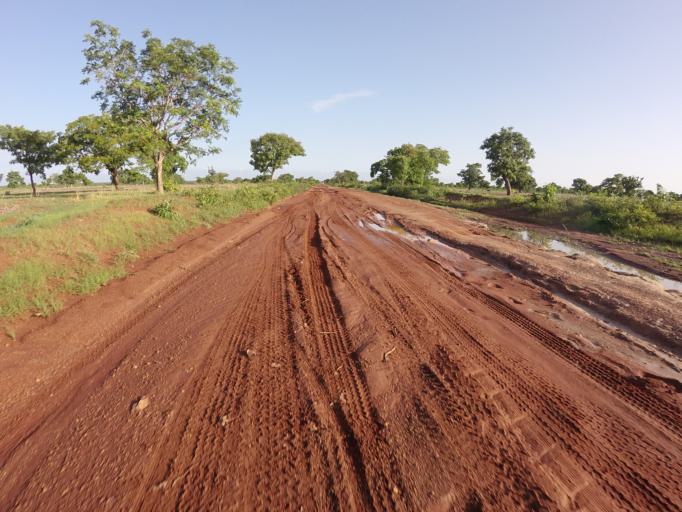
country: TG
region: Savanes
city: Sansanne-Mango
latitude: 10.3720
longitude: -0.0940
